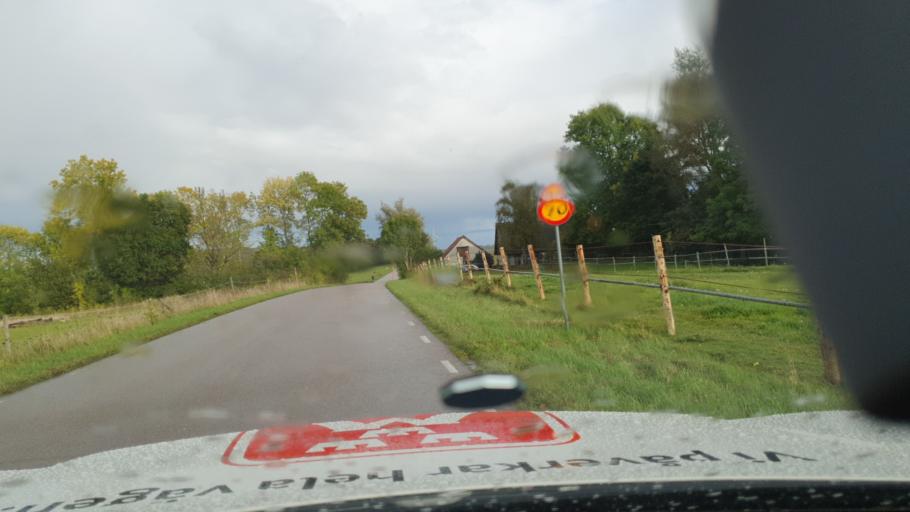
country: SE
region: Skane
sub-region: Malmo
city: Oxie
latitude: 55.5243
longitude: 13.1053
